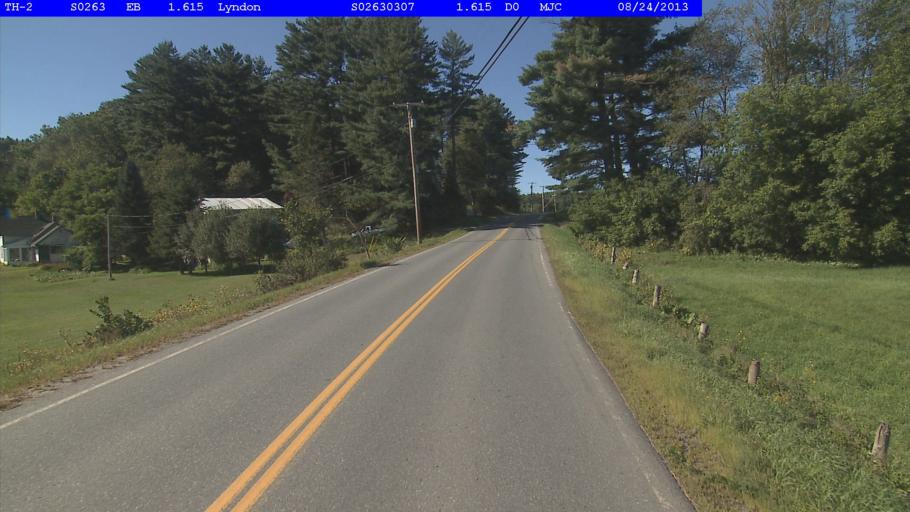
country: US
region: Vermont
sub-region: Caledonia County
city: Lyndon
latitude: 44.5079
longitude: -71.9916
